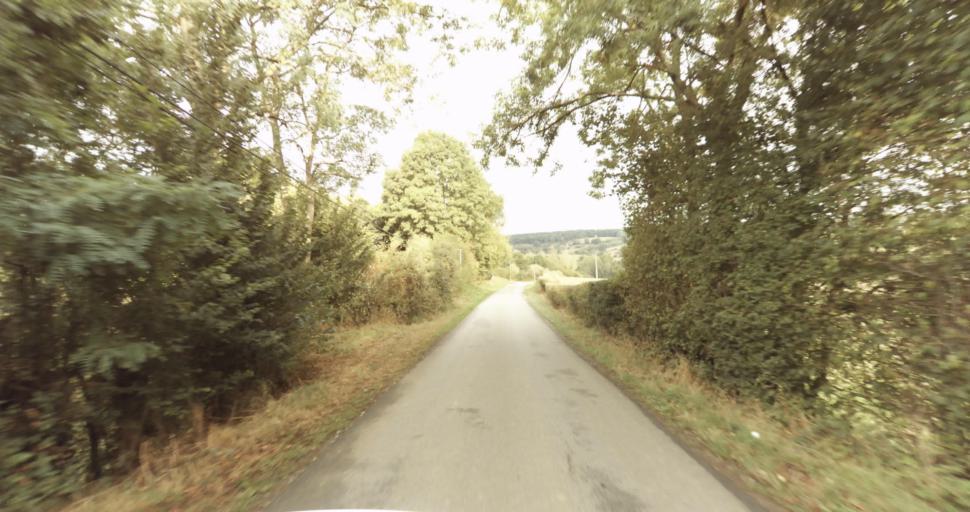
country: FR
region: Lower Normandy
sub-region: Departement de l'Orne
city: Trun
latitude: 48.9222
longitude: 0.0935
